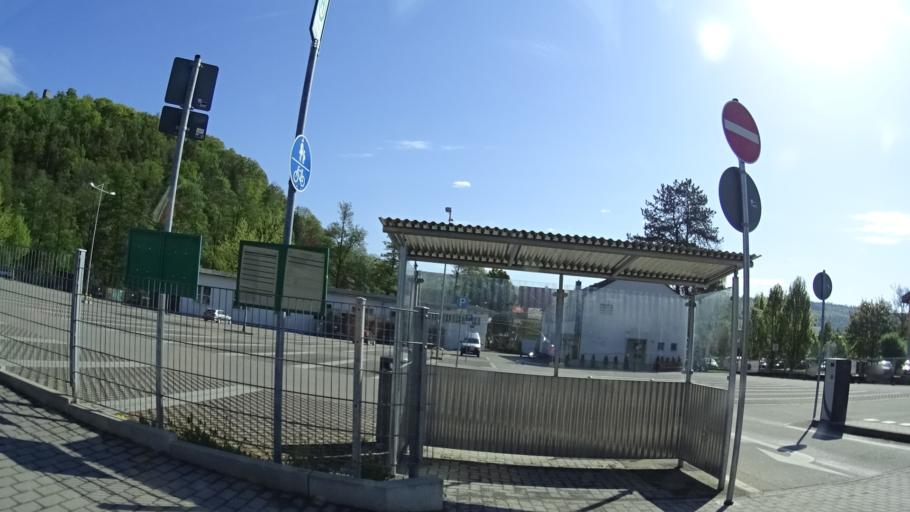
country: DE
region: Baden-Wuerttemberg
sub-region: Karlsruhe Region
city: Nagold
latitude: 48.5493
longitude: 8.7144
